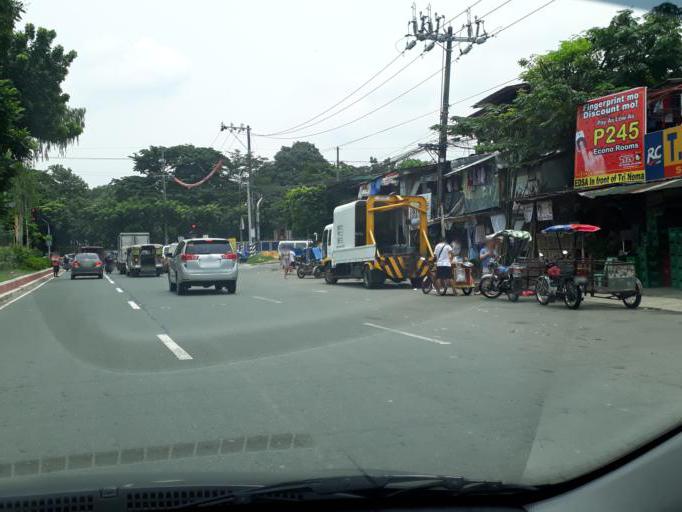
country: PH
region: Calabarzon
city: Bagong Pagasa
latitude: 14.6529
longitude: 121.0388
